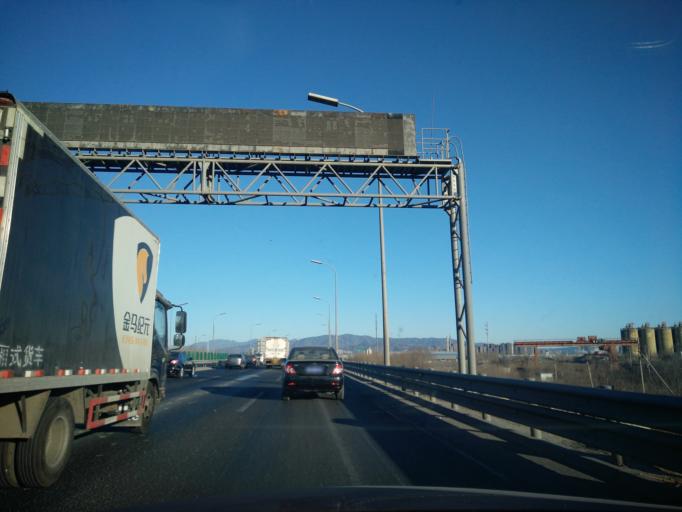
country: CN
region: Beijing
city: Lugu
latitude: 39.8693
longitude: 116.2045
